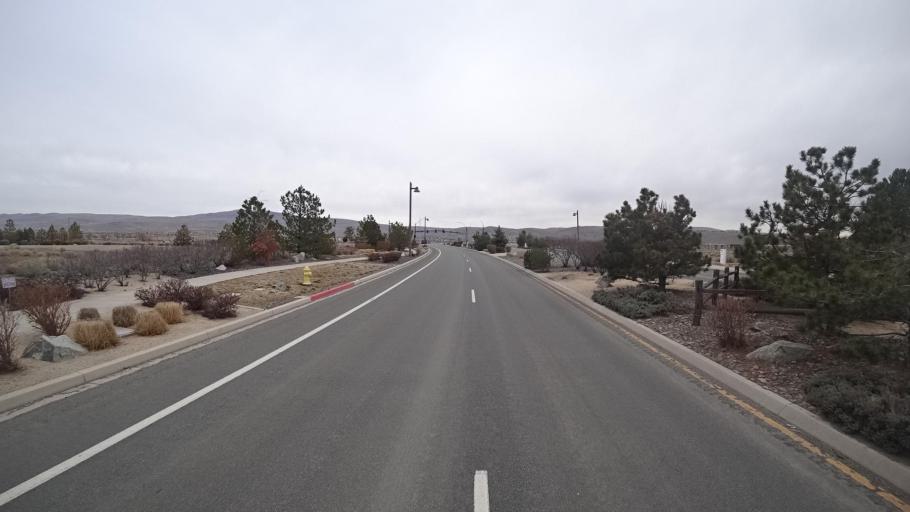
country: US
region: Nevada
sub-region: Washoe County
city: Spanish Springs
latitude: 39.6154
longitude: -119.7260
